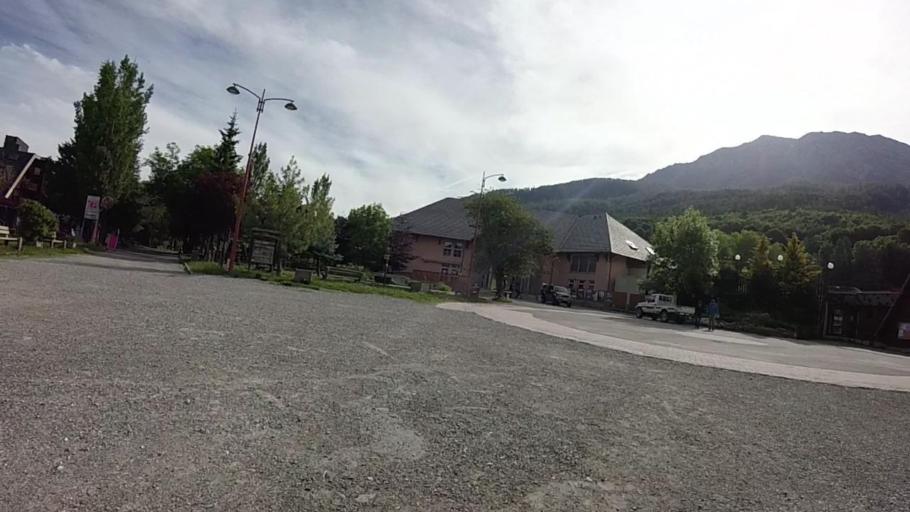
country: FR
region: Provence-Alpes-Cote d'Azur
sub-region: Departement des Alpes-de-Haute-Provence
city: Seyne-les-Alpes
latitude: 44.4118
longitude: 6.3508
